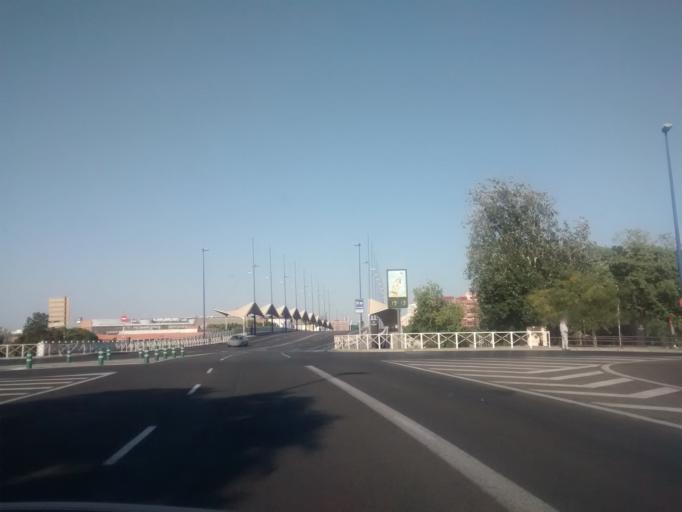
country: ES
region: Andalusia
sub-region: Provincia de Sevilla
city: Camas
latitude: 37.3900
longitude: -6.0084
